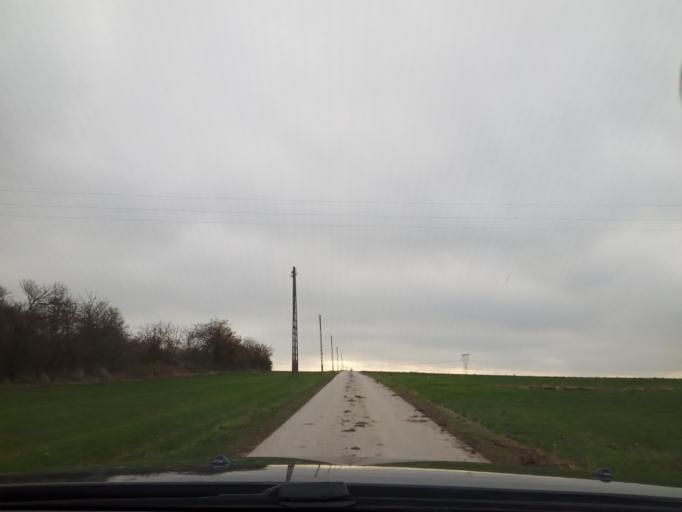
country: PL
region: Swietokrzyskie
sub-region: Powiat jedrzejowski
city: Imielno
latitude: 50.6193
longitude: 20.3952
